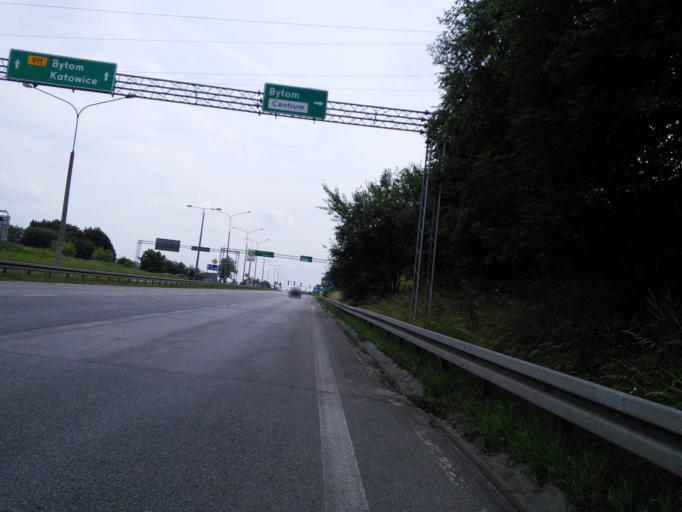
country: PL
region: Silesian Voivodeship
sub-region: Bytom
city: Bytom
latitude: 50.3630
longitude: 18.9382
